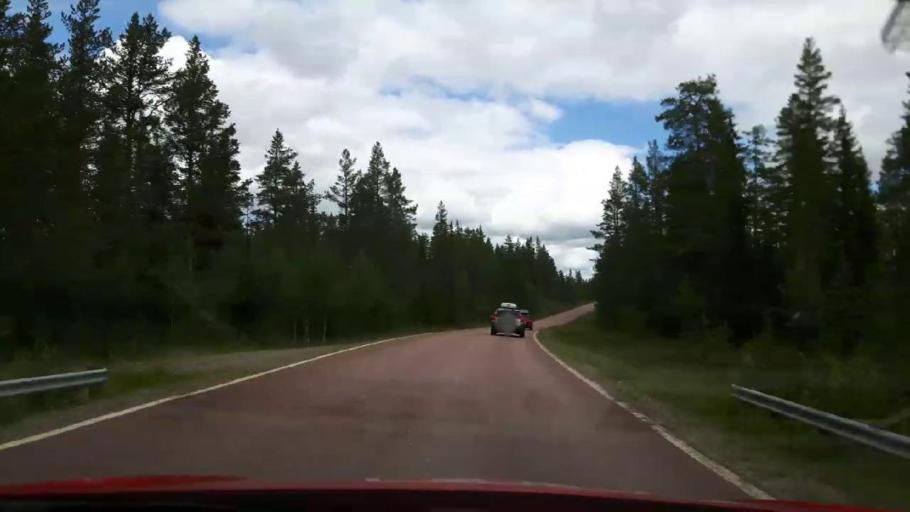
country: NO
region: Hedmark
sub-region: Trysil
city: Innbygda
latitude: 61.8653
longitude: 12.9532
